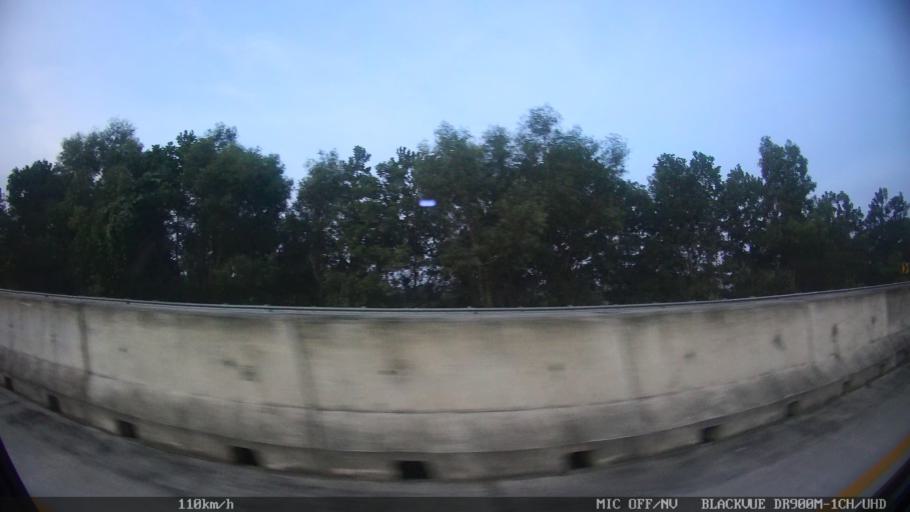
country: ID
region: Lampung
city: Pasuruan
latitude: -5.7360
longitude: 105.6885
